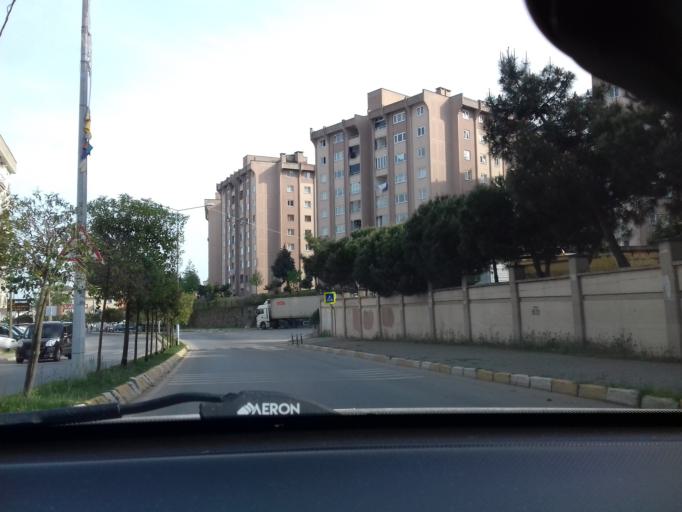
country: TR
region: Istanbul
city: Pendik
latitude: 40.9110
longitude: 29.2790
